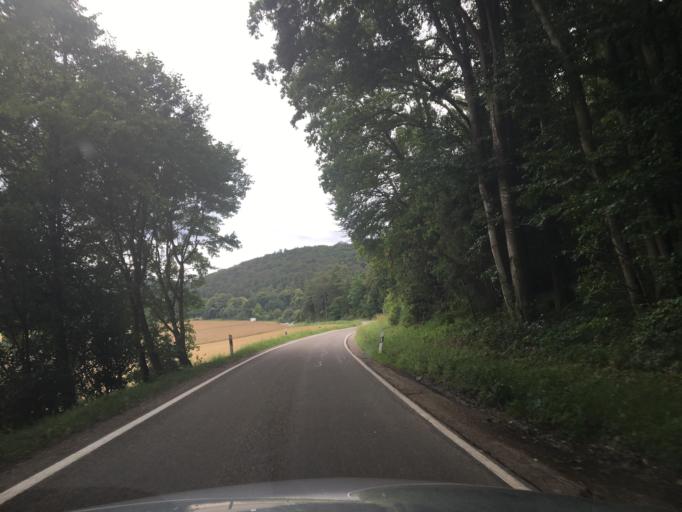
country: DE
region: Bavaria
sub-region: Regierungsbezirk Mittelfranken
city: Greding
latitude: 49.0164
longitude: 11.3702
